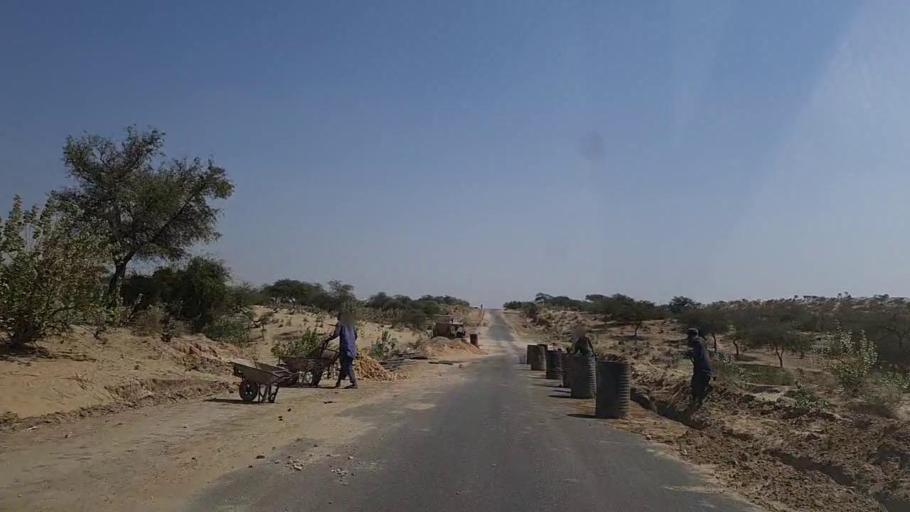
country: PK
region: Sindh
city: Diplo
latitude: 24.4837
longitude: 69.4709
